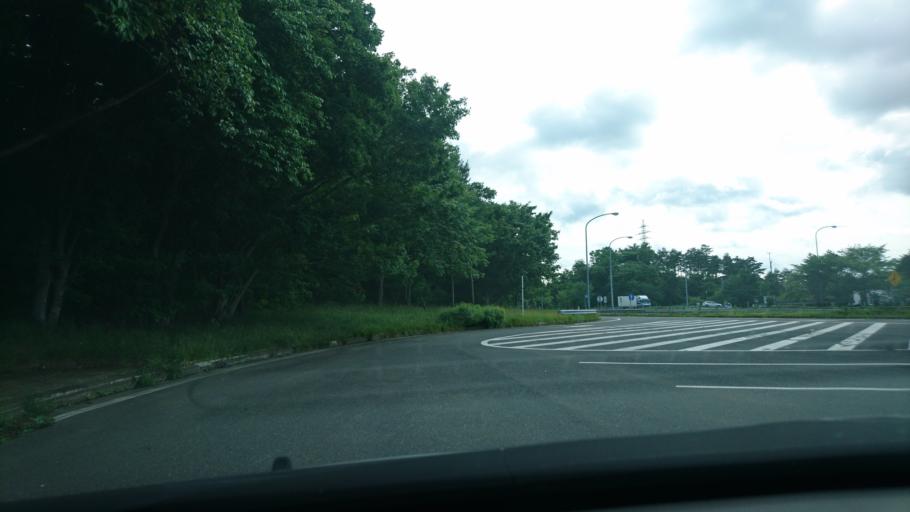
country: JP
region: Aomori
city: Hachinohe
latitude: 40.4443
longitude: 141.4503
